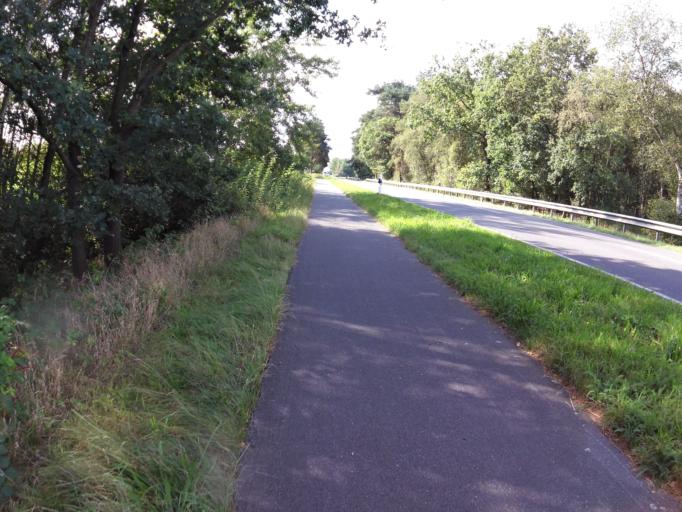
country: DE
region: Lower Saxony
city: Bremervorde
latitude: 53.4630
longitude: 9.1411
